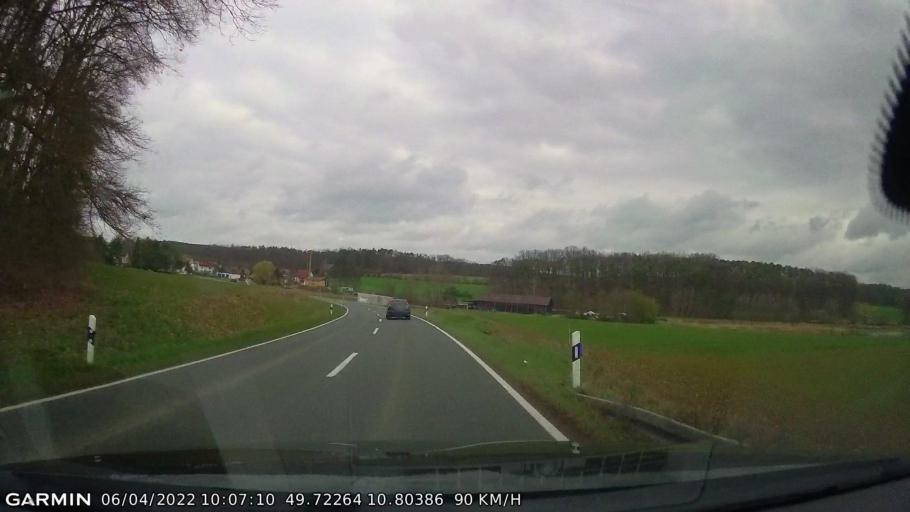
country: DE
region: Bavaria
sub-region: Regierungsbezirk Mittelfranken
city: Hochstadt an der Aisch
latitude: 49.7228
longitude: 10.8039
